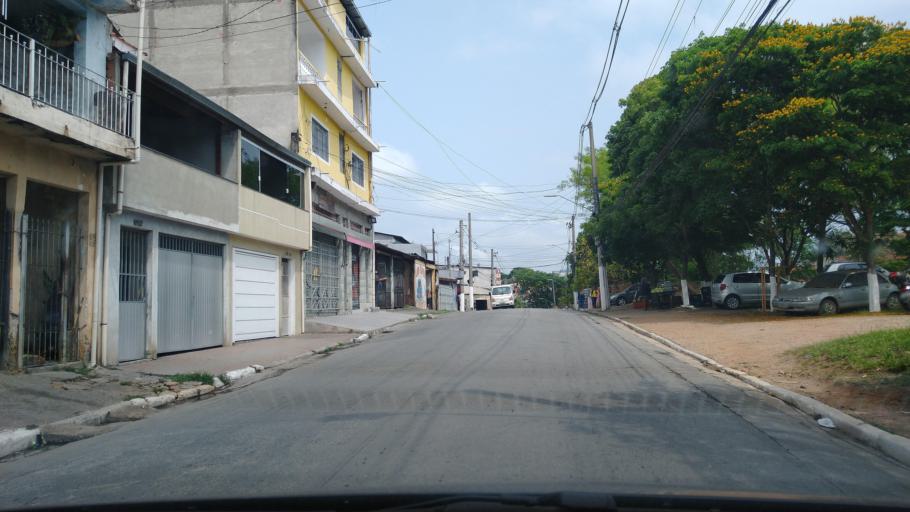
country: BR
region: Sao Paulo
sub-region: Caieiras
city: Caieiras
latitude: -23.4396
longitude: -46.7099
